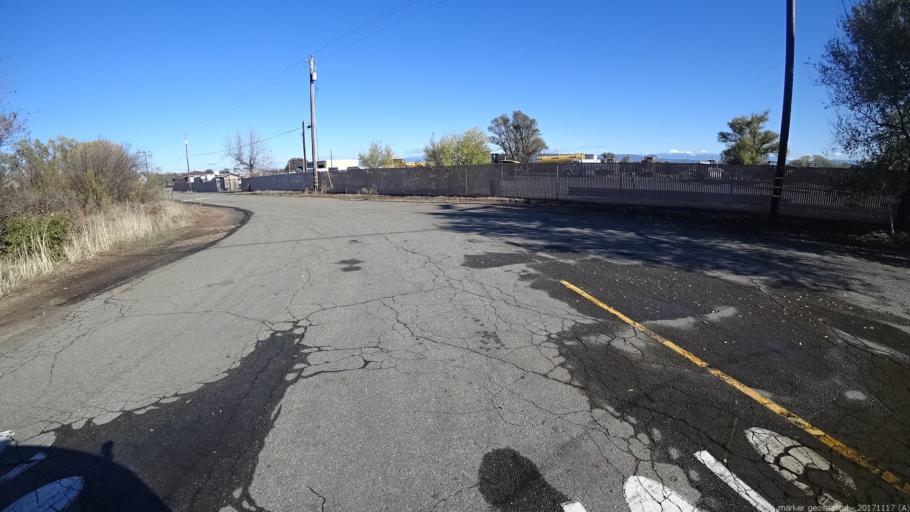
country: US
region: California
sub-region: Shasta County
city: Cottonwood
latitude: 40.4226
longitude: -122.2596
